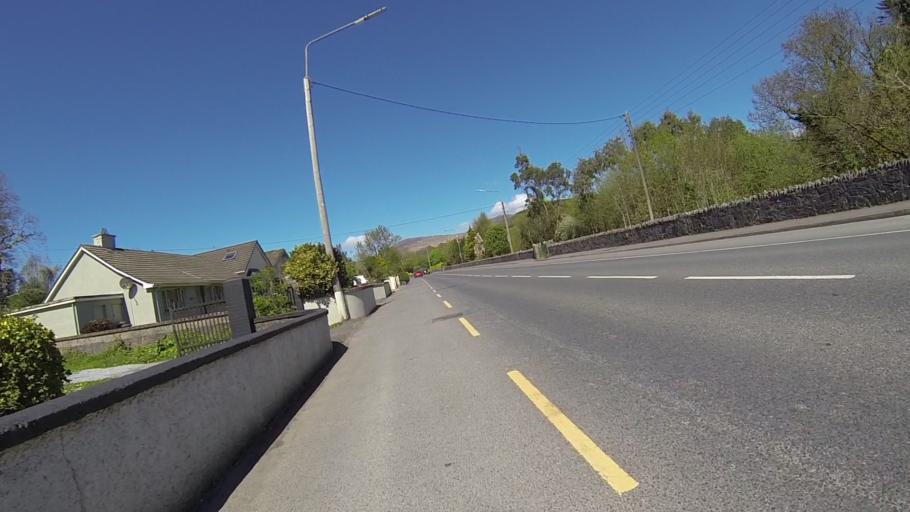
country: IE
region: Munster
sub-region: Ciarrai
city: Kenmare
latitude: 51.8822
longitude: -9.5851
